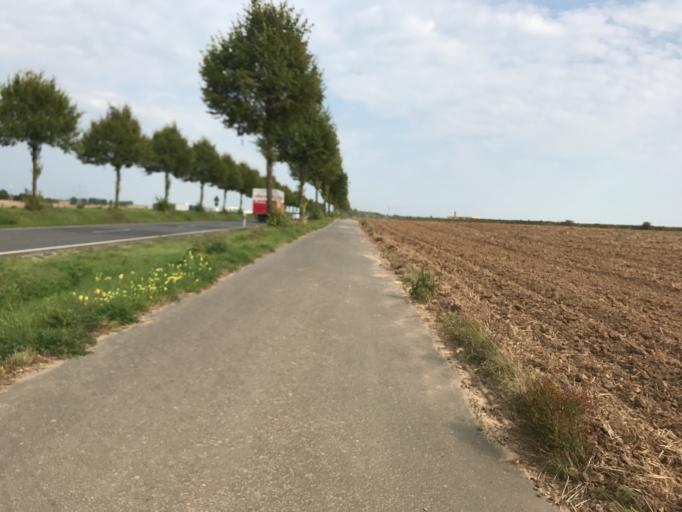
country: DE
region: Rheinland-Pfalz
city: Gau-Bischofsheim
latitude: 49.9514
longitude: 8.2551
